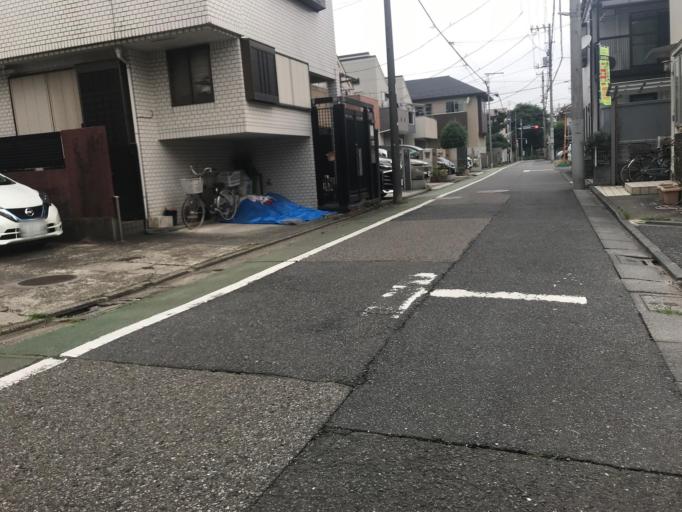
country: JP
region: Saitama
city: Wako
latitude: 35.7320
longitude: 139.6204
